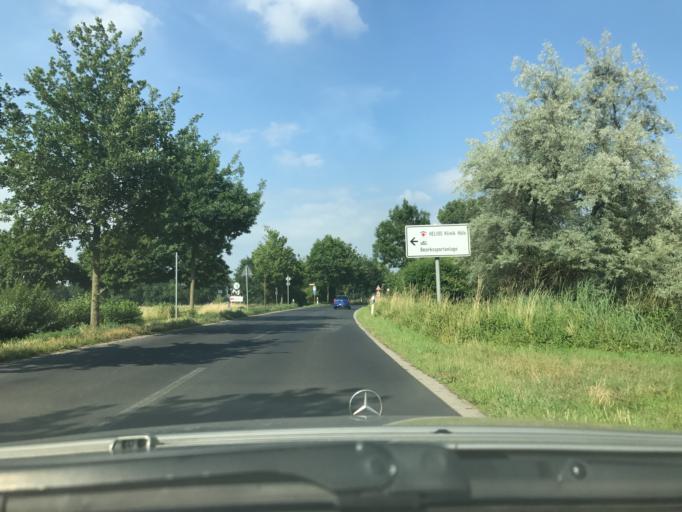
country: DE
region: North Rhine-Westphalia
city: Tonisvorst
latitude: 51.3723
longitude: 6.5264
